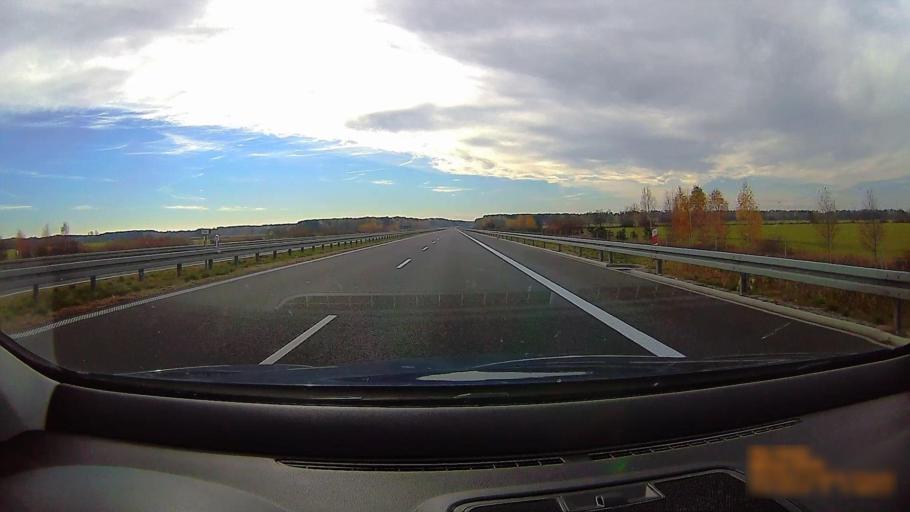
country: PL
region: Greater Poland Voivodeship
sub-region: Powiat ostrowski
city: Przygodzice
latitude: 51.5802
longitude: 17.8492
